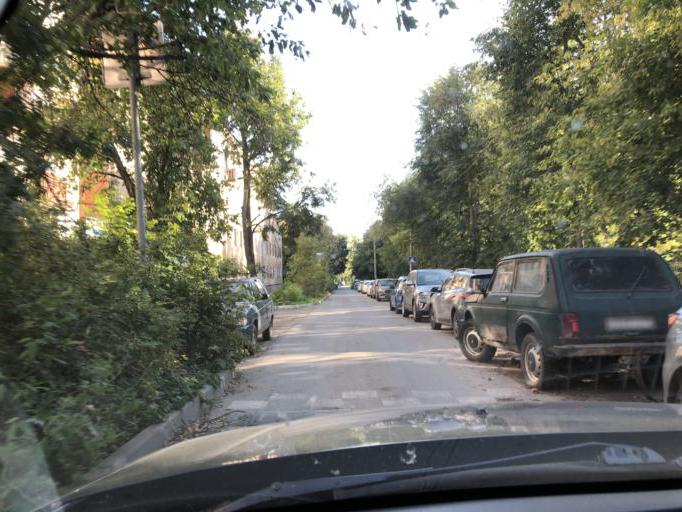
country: RU
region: Tula
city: Tula
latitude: 54.2102
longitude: 37.6072
